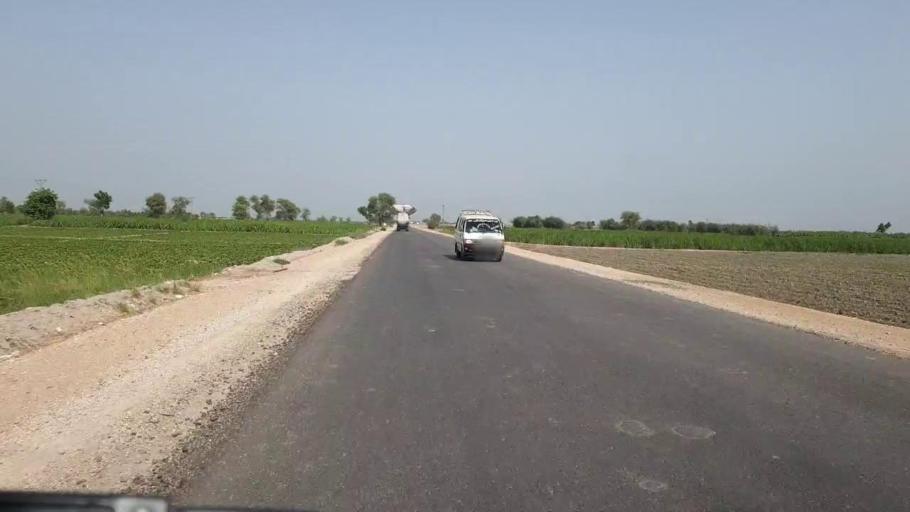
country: PK
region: Sindh
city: Sakrand
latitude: 26.2689
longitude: 68.1660
